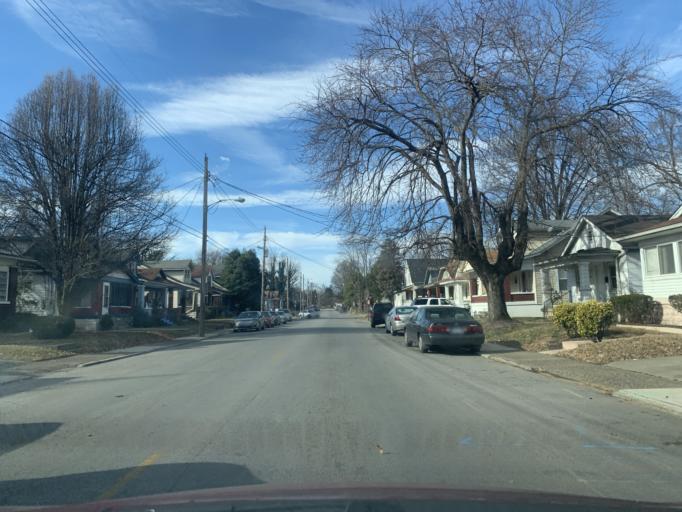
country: US
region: Kentucky
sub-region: Jefferson County
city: Shively
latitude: 38.2292
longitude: -85.7941
